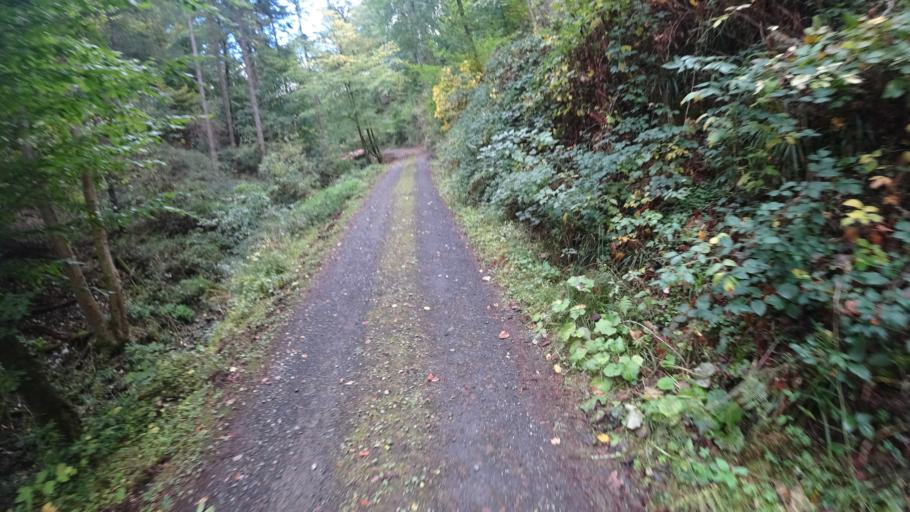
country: DE
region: Rheinland-Pfalz
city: Kratzenburg
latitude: 50.2207
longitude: 7.5434
